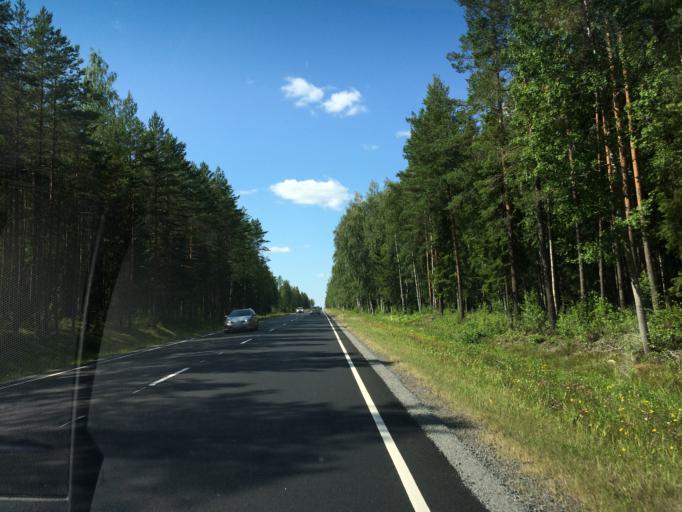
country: FI
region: Pirkanmaa
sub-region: Lounais-Pirkanmaa
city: Kiikoinen
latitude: 61.4742
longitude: 22.4886
